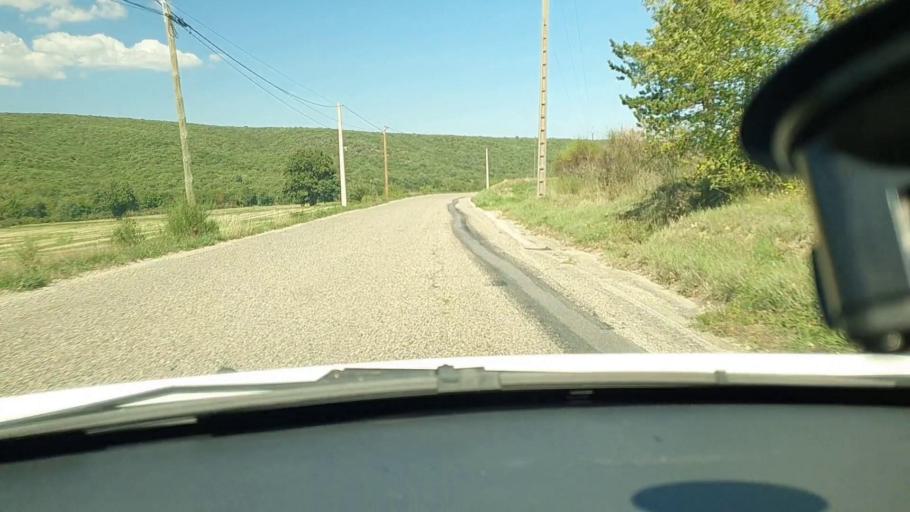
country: FR
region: Languedoc-Roussillon
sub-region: Departement du Gard
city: Goudargues
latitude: 44.1450
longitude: 4.4483
